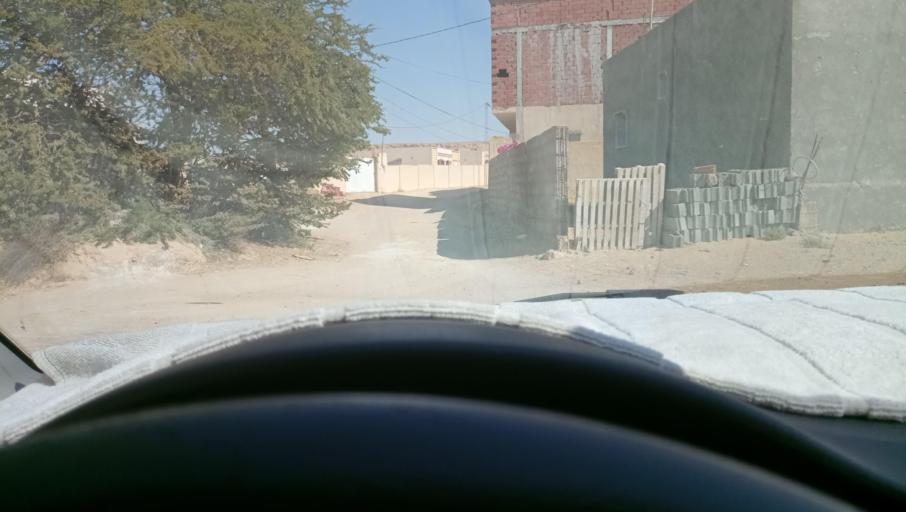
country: TN
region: Tataouine
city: Tataouine
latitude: 32.9824
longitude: 10.3816
